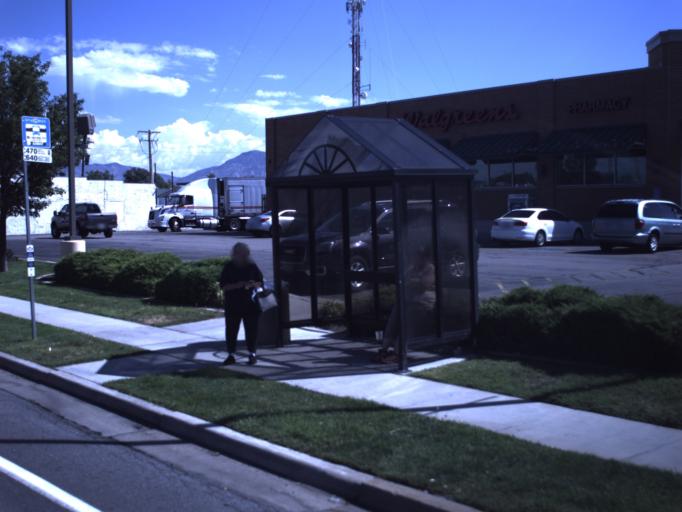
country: US
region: Utah
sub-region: Weber County
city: Roy
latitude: 41.1625
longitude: -112.0259
